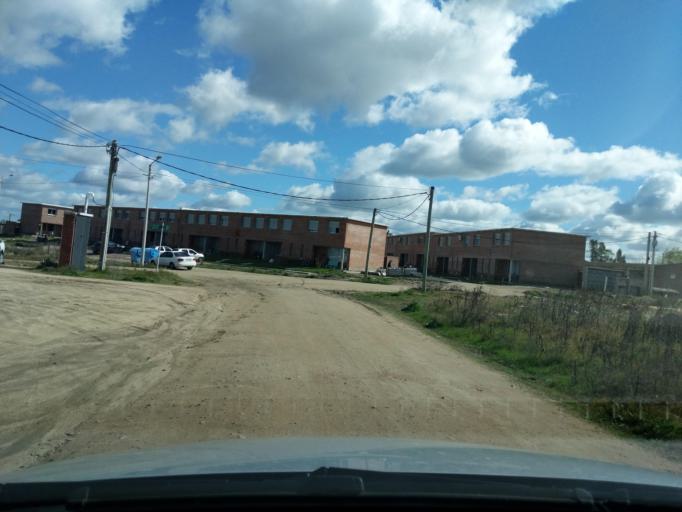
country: UY
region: Florida
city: Florida
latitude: -34.0802
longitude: -56.2245
